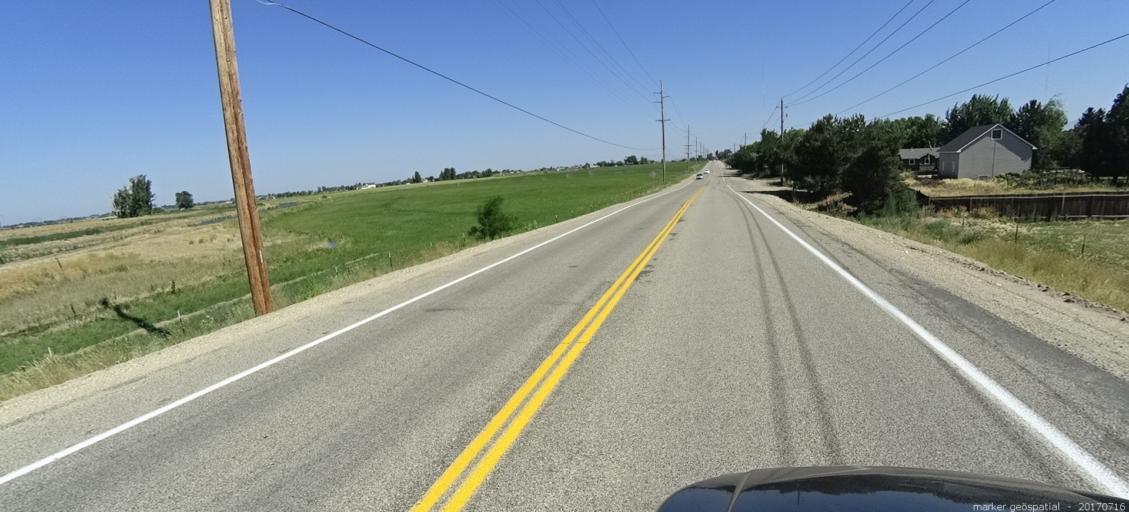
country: US
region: Idaho
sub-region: Ada County
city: Kuna
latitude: 43.5084
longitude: -116.3344
